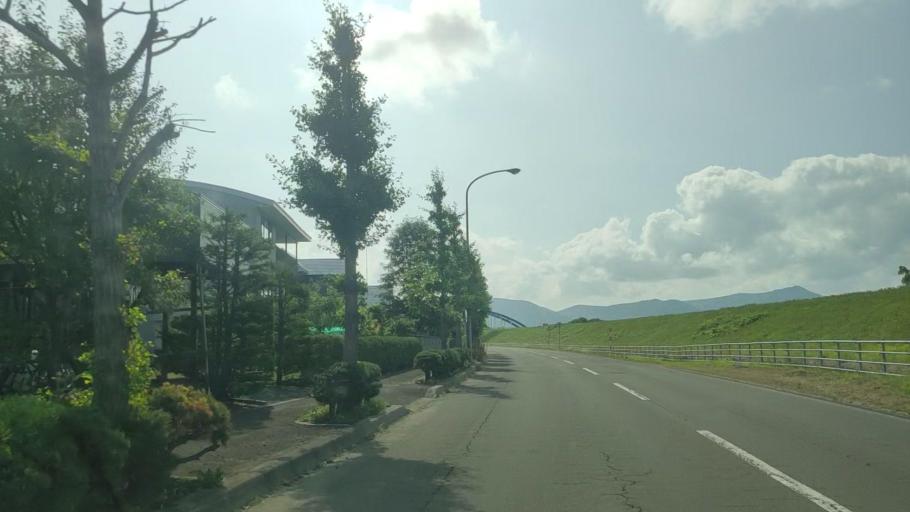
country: JP
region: Hokkaido
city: Shimo-furano
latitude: 43.3406
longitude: 142.3799
